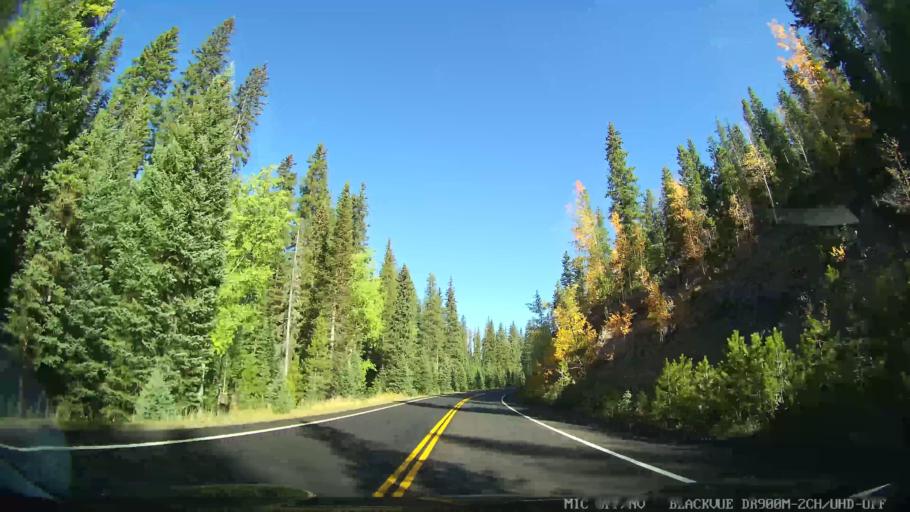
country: US
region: Colorado
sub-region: Grand County
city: Granby
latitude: 40.2988
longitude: -105.8427
